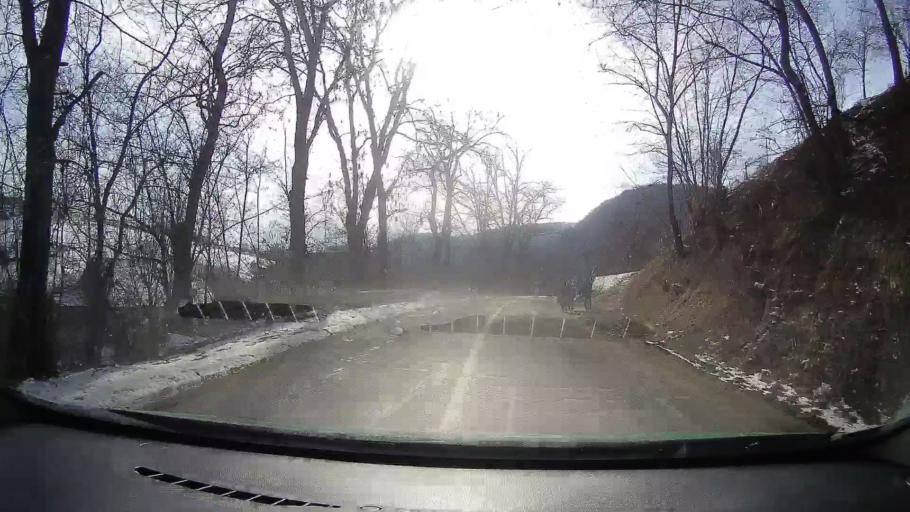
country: RO
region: Mures
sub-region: Municipiul Sighisoara
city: Sighisoara
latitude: 46.2034
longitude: 24.7740
